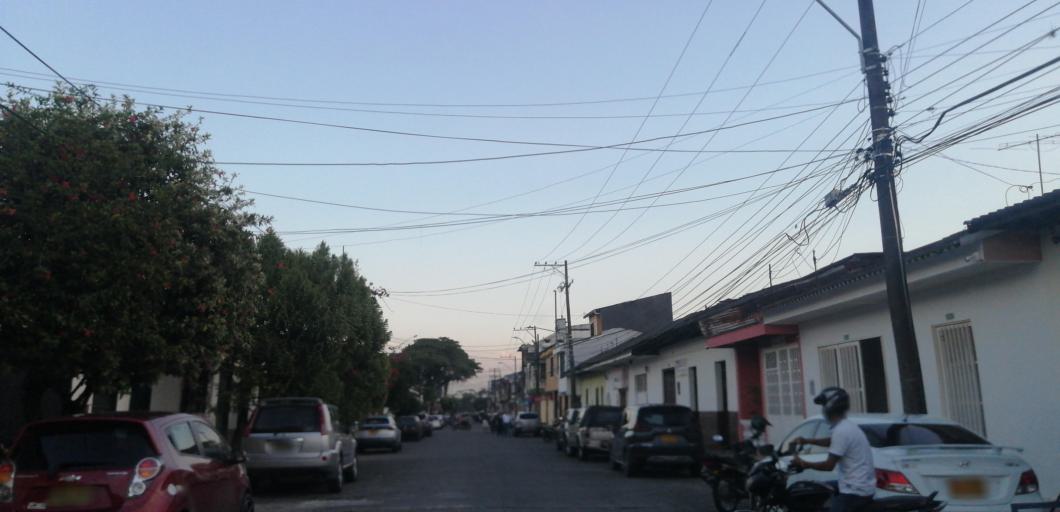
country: CO
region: Meta
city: Acacias
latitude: 3.9883
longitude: -73.7594
